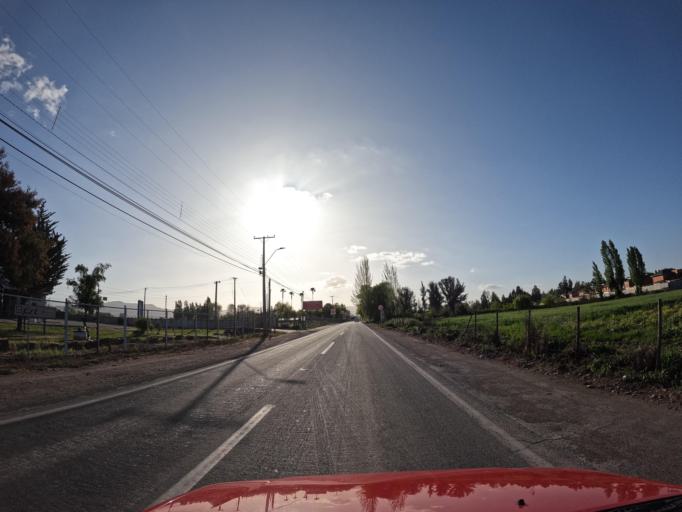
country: CL
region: O'Higgins
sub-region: Provincia de Colchagua
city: Santa Cruz
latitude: -34.6499
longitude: -71.3528
